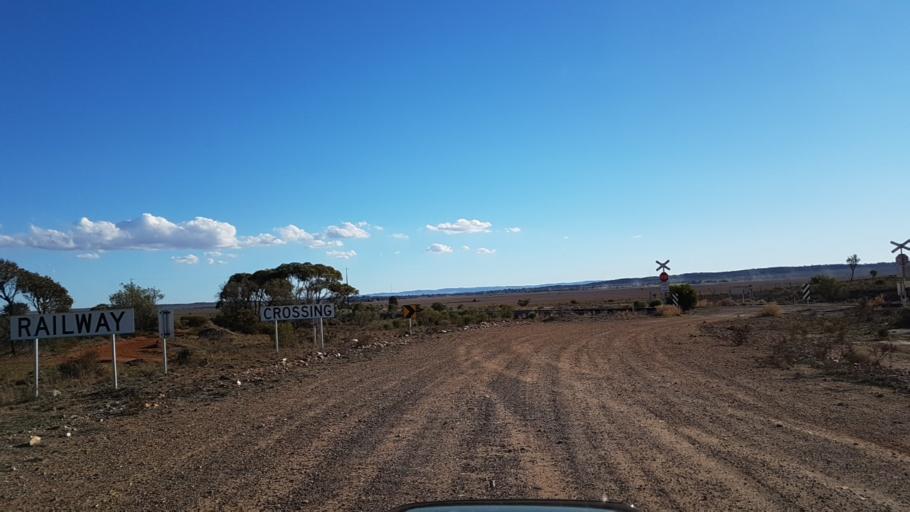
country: AU
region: South Australia
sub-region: Peterborough
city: Peterborough
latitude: -32.9598
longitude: 138.8929
